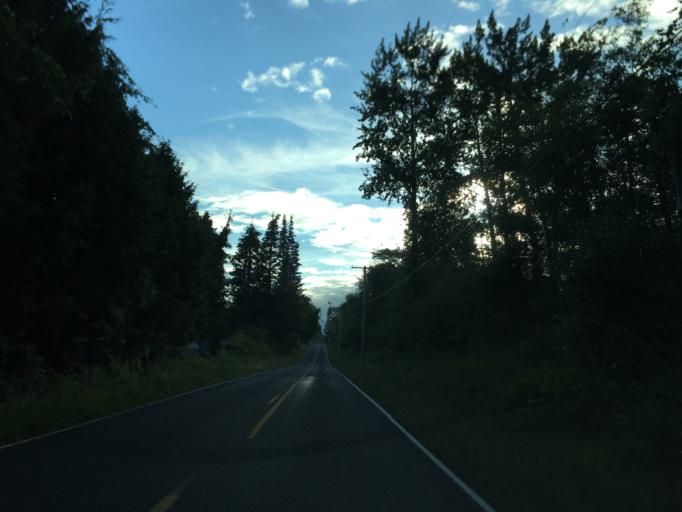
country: US
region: Washington
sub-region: Whatcom County
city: Birch Bay
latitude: 48.9439
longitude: -122.7955
